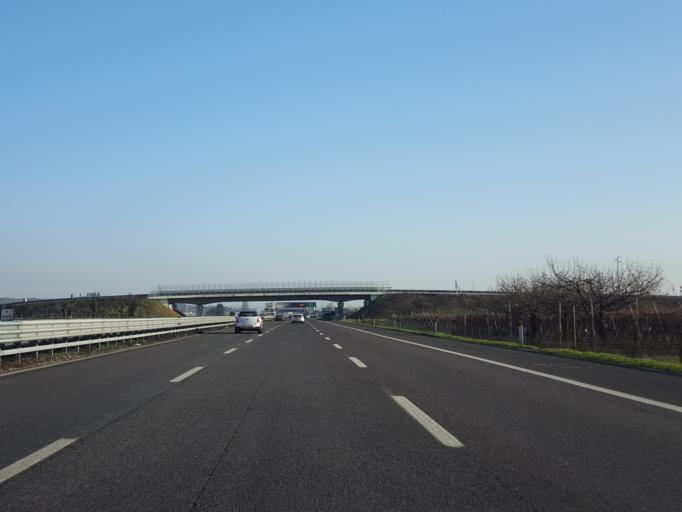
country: IT
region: Veneto
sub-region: Provincia di Verona
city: Soave
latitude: 45.4123
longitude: 11.2192
